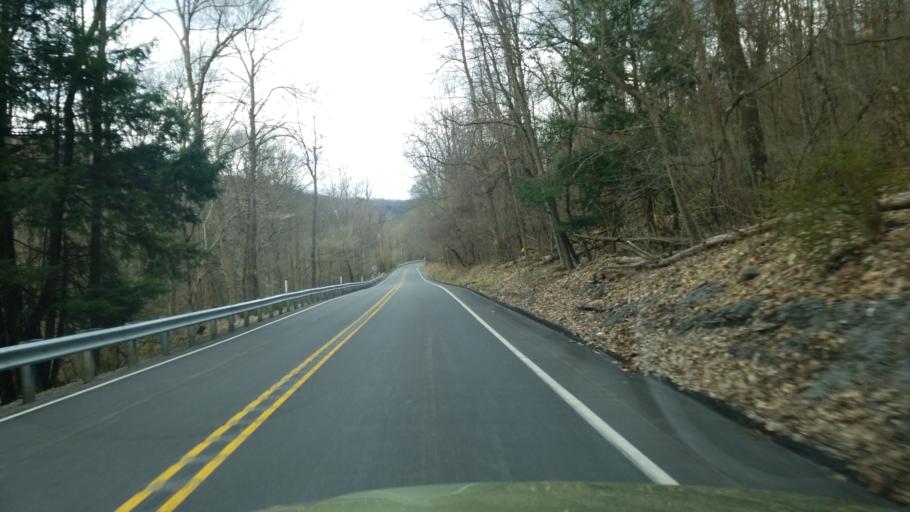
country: US
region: Pennsylvania
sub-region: Clearfield County
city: Curwensville
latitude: 40.8659
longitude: -78.4446
